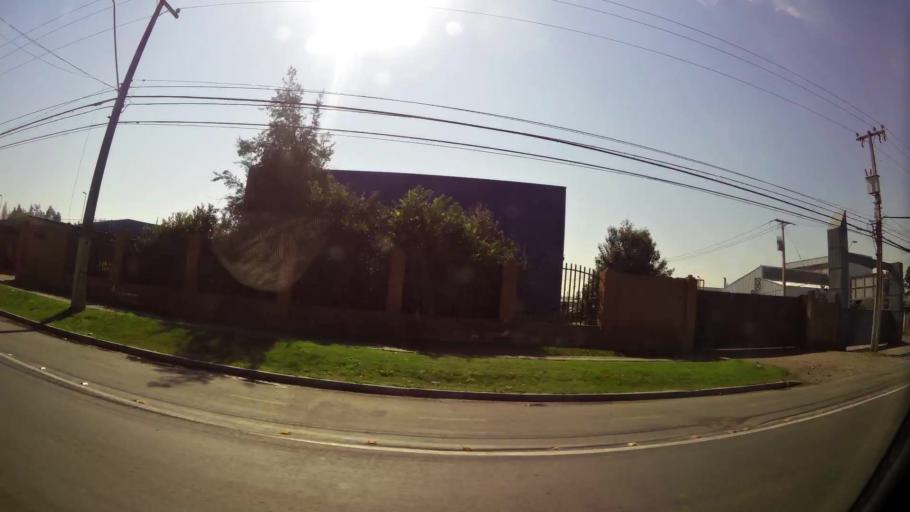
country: CL
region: Santiago Metropolitan
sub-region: Provincia de Talagante
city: Penaflor
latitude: -33.5604
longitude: -70.8230
